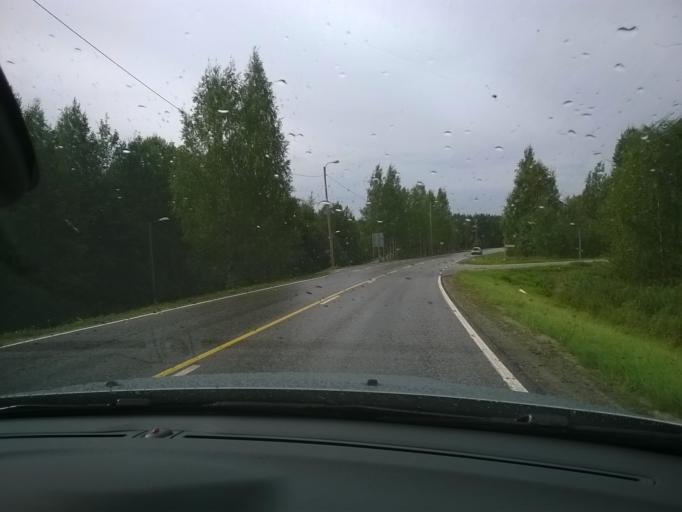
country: FI
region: Kainuu
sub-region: Kehys-Kainuu
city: Kuhmo
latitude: 64.1186
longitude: 29.5716
